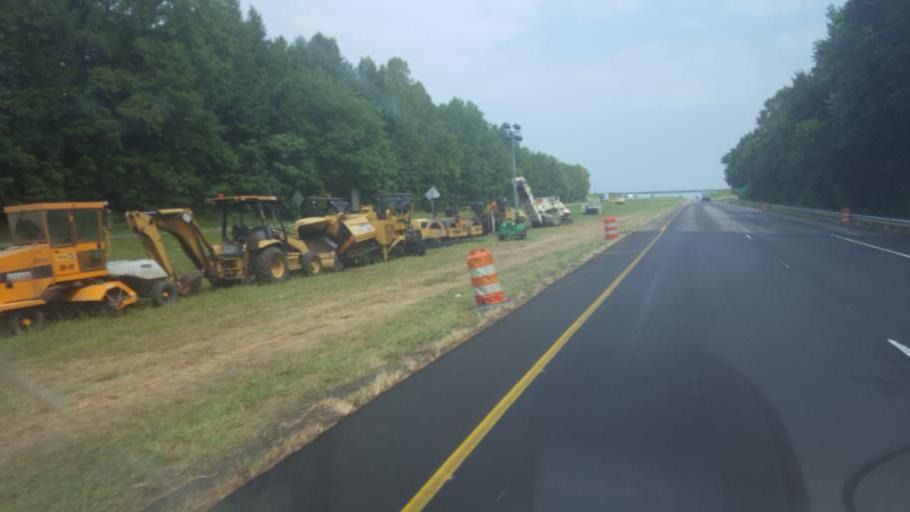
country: US
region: North Carolina
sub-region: Iredell County
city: Statesville
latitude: 35.9107
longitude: -80.8541
